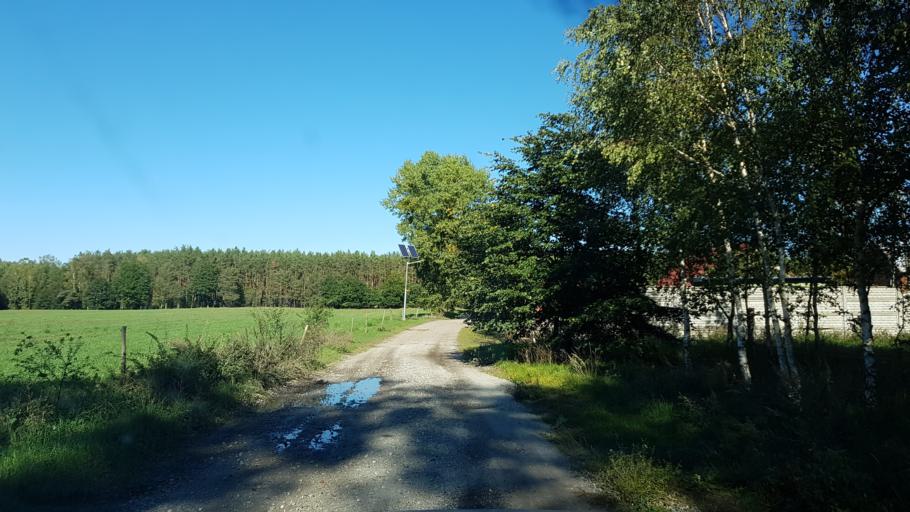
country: PL
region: Lubusz
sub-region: Powiat gorzowski
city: Lubiszyn
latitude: 52.8388
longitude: 14.9295
